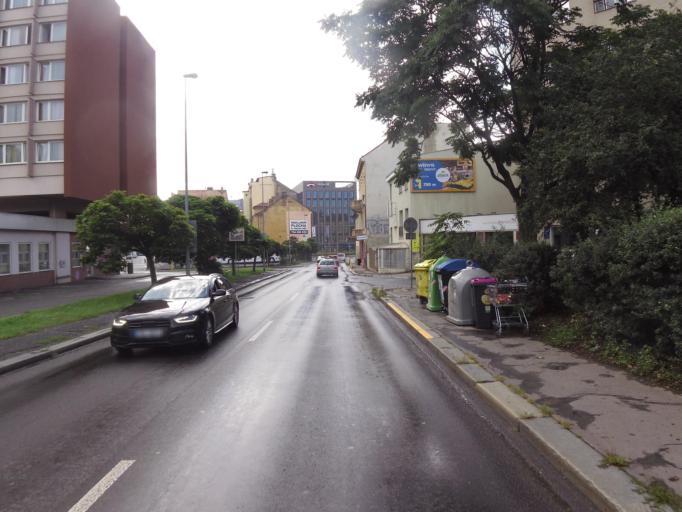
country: CZ
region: Praha
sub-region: Praha 8
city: Liben
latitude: 50.0993
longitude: 14.4712
